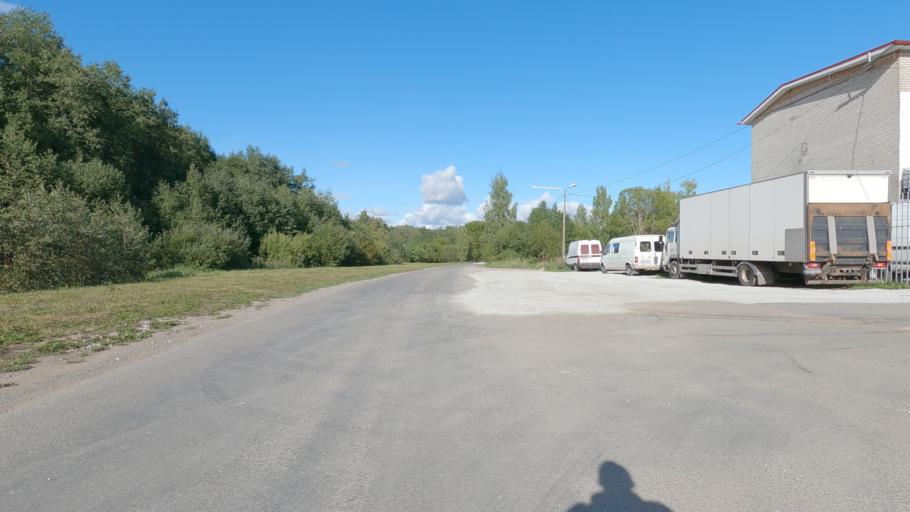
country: EE
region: Raplamaa
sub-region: Rapla vald
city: Rapla
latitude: 58.9965
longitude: 24.8242
